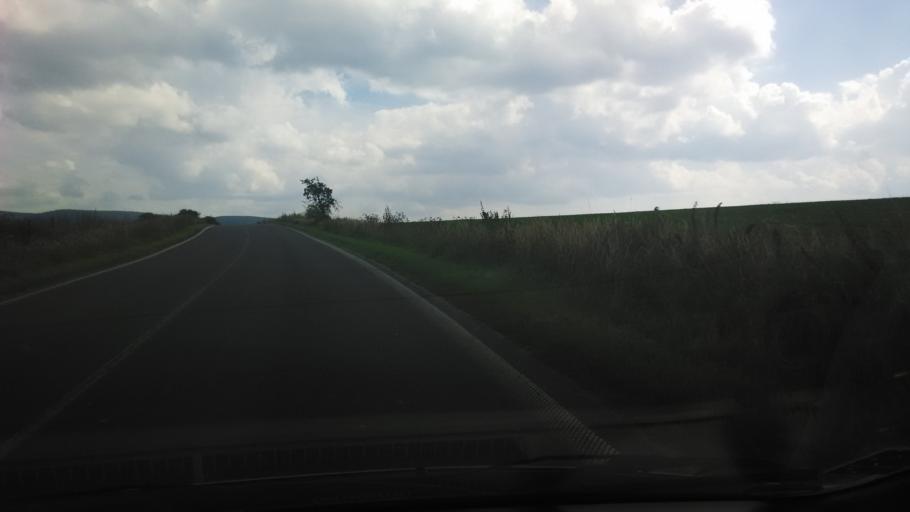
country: SK
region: Banskobystricky
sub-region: Okres Ziar nad Hronom
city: Kremnica
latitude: 48.8378
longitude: 18.8712
